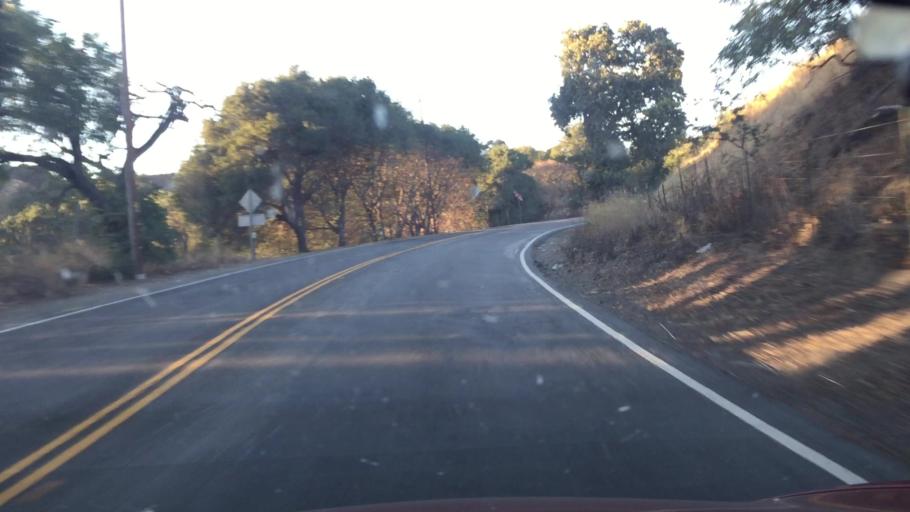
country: US
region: California
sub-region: Alameda County
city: Pleasanton
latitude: 37.5941
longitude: -121.8821
